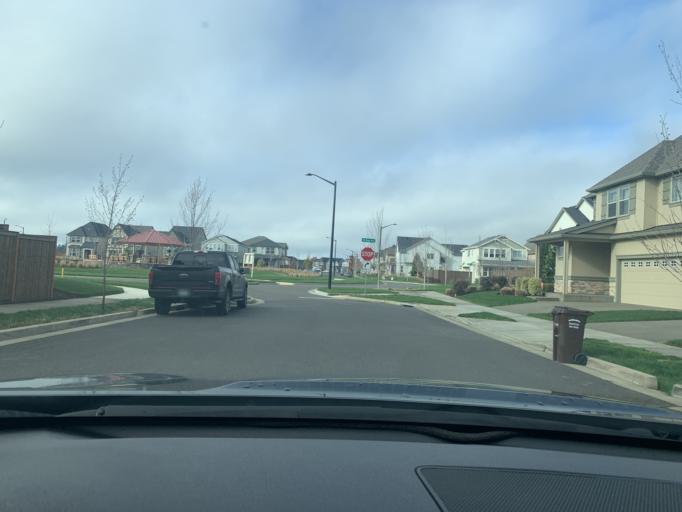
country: US
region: Oregon
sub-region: Washington County
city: North Plains
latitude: 45.5943
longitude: -122.9735
